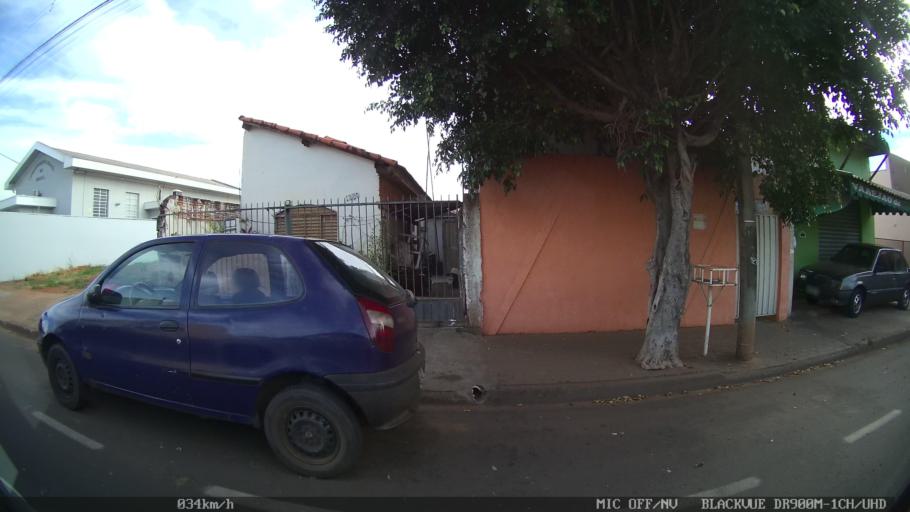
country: BR
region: Sao Paulo
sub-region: Catanduva
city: Catanduva
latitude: -21.1403
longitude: -49.0018
